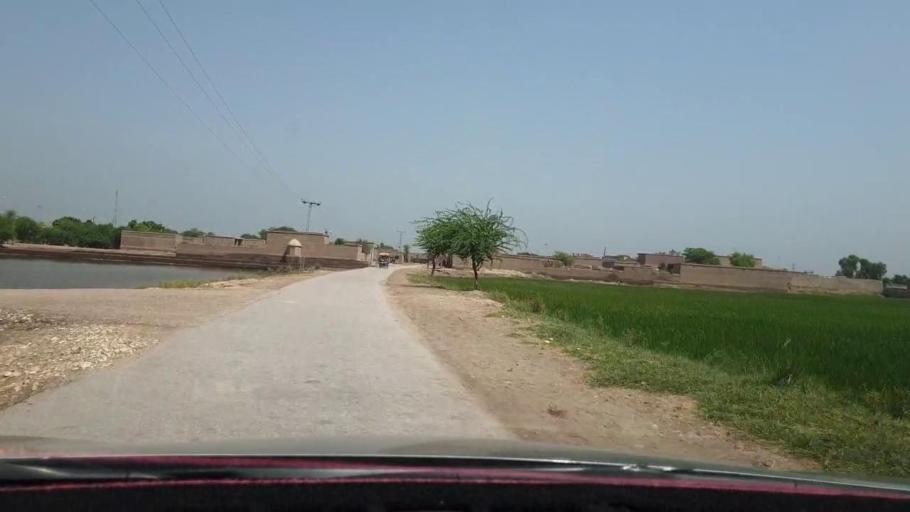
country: PK
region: Sindh
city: Warah
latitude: 27.4419
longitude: 67.7774
